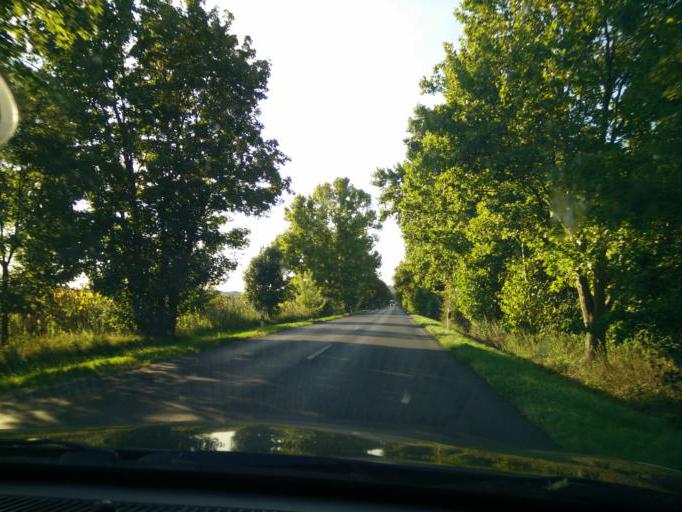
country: HU
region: Pest
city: Zsambek
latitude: 47.5300
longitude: 18.7342
